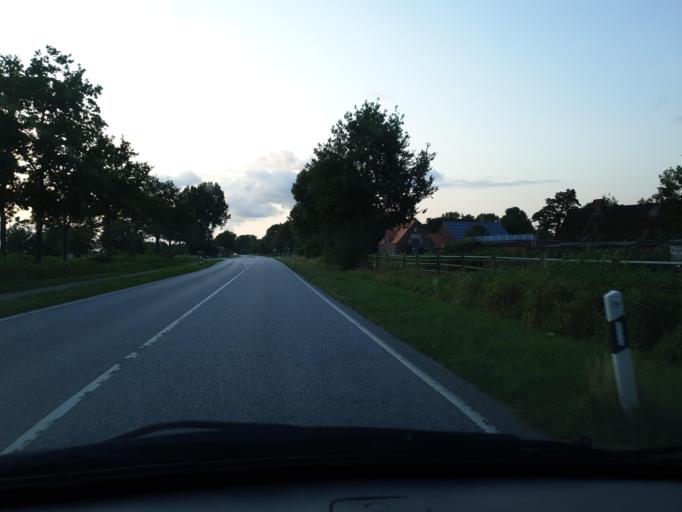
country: DE
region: Schleswig-Holstein
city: Schmedeswurth
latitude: 53.9167
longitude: 9.0495
